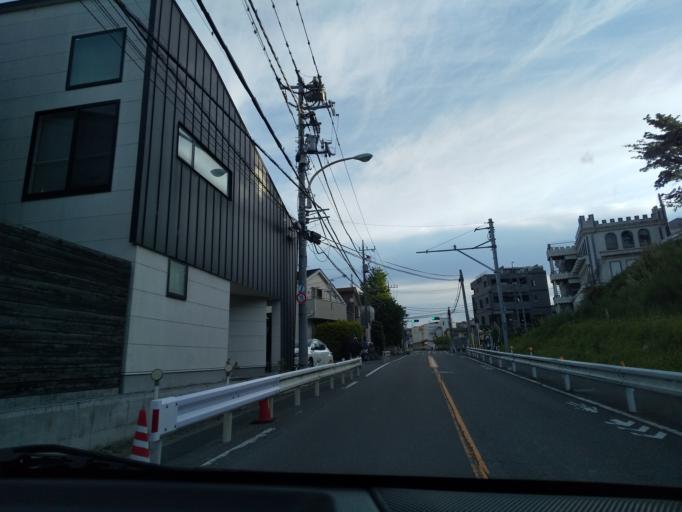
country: JP
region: Tokyo
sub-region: Machida-shi
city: Machida
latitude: 35.5637
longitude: 139.4521
